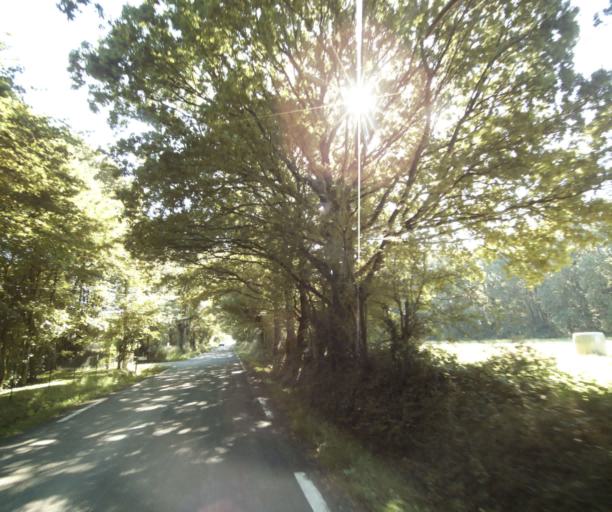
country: FR
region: Pays de la Loire
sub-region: Departement de la Mayenne
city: Laval
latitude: 48.0395
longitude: -0.7334
